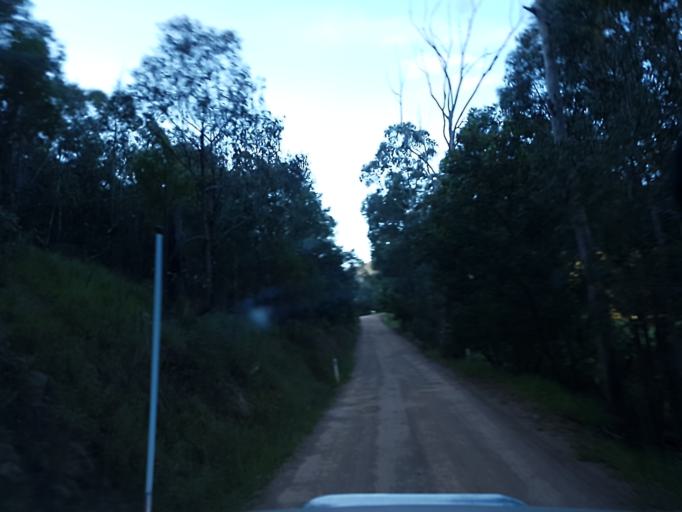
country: AU
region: Victoria
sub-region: Wellington
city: Heyfield
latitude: -37.4087
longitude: 147.0861
